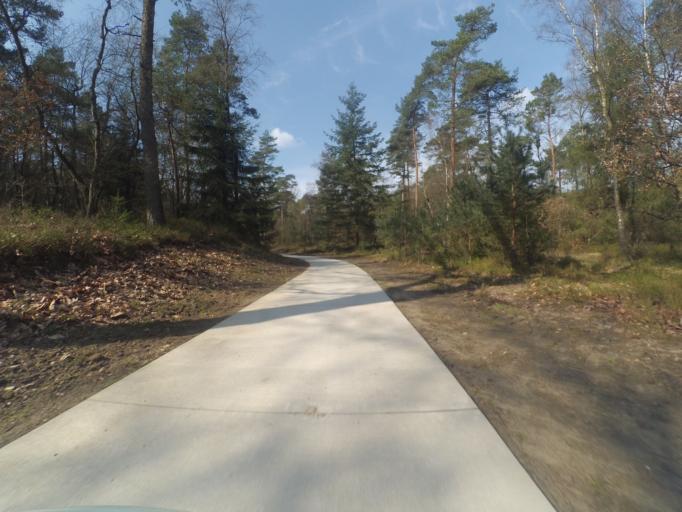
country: NL
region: Gelderland
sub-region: Gemeente Apeldoorn
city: Beekbergen
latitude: 52.1547
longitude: 5.9155
